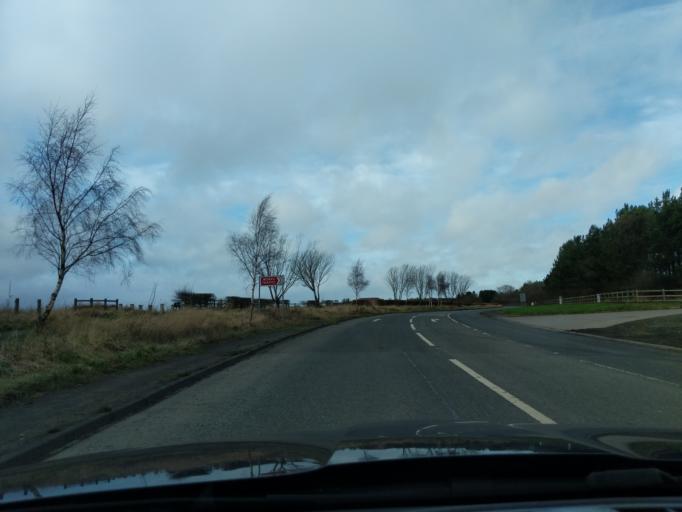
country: GB
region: England
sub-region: Northumberland
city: Lynemouth
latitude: 55.2057
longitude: -1.5333
